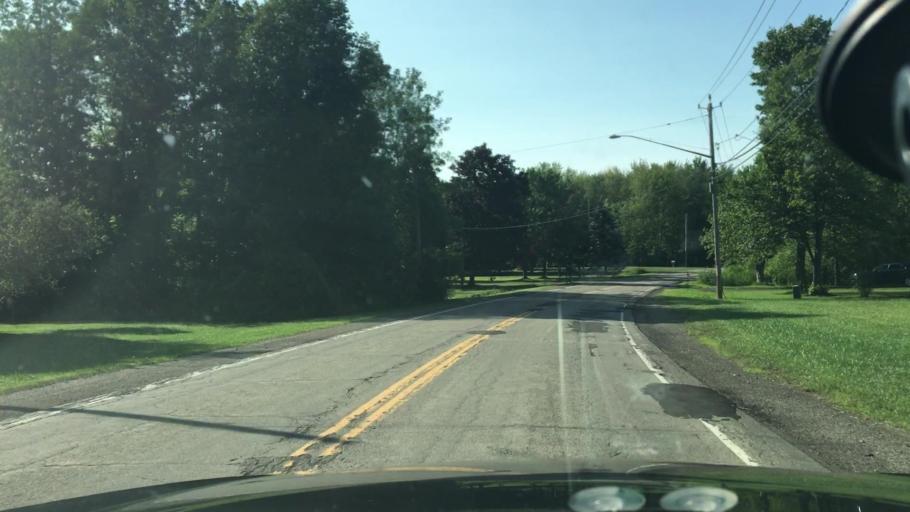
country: US
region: New York
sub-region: Erie County
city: Angola
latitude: 42.6249
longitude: -79.0257
